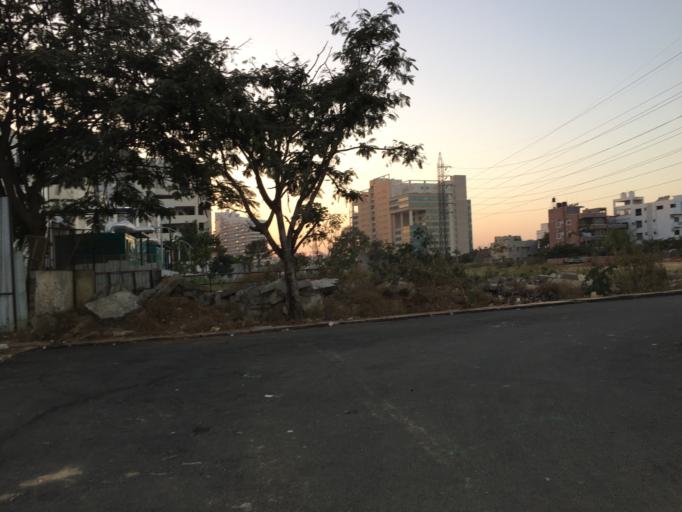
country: IN
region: Karnataka
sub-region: Bangalore Urban
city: Yelahanka
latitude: 13.0511
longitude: 77.6221
